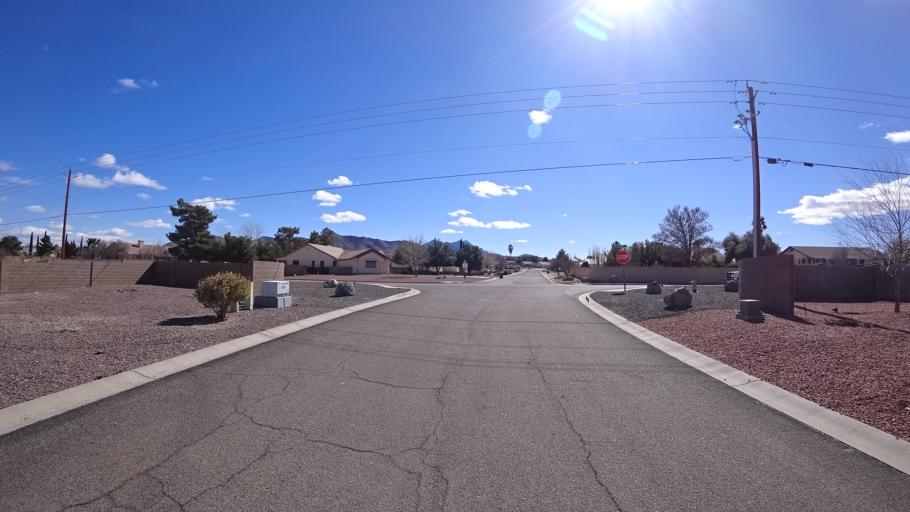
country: US
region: Arizona
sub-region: Mohave County
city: Kingman
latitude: 35.2034
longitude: -113.9710
